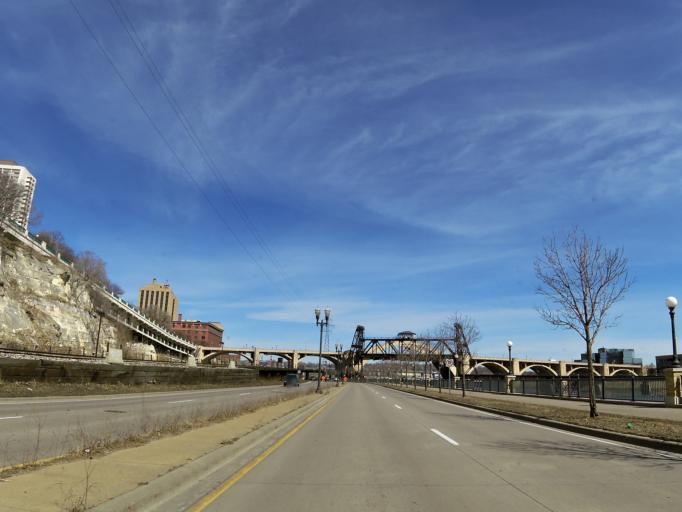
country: US
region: Minnesota
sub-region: Ramsey County
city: Saint Paul
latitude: 44.9434
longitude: -93.0919
